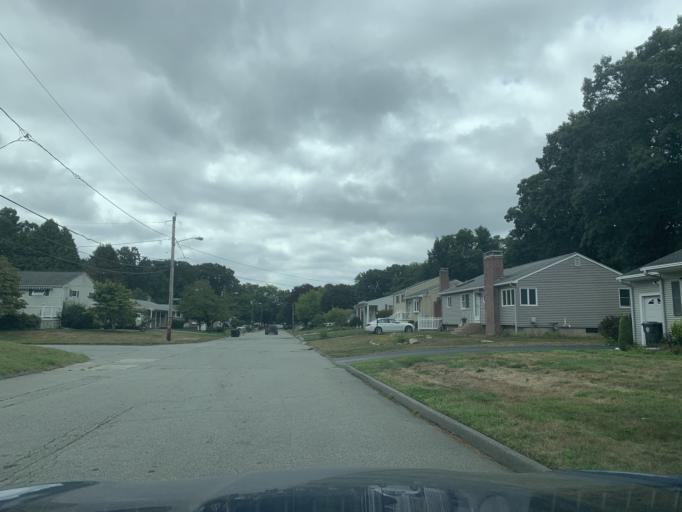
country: US
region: Rhode Island
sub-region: Kent County
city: East Greenwich
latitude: 41.6886
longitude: -71.4740
